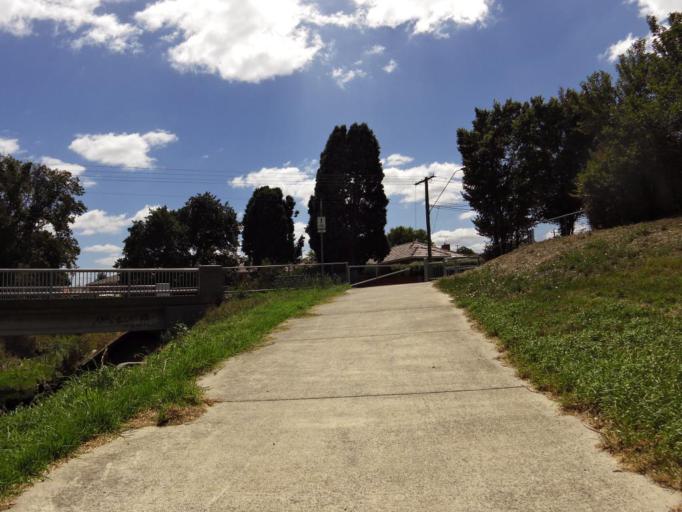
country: AU
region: Victoria
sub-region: Whittlesea
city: Thomastown
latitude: -37.6824
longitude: 145.0073
